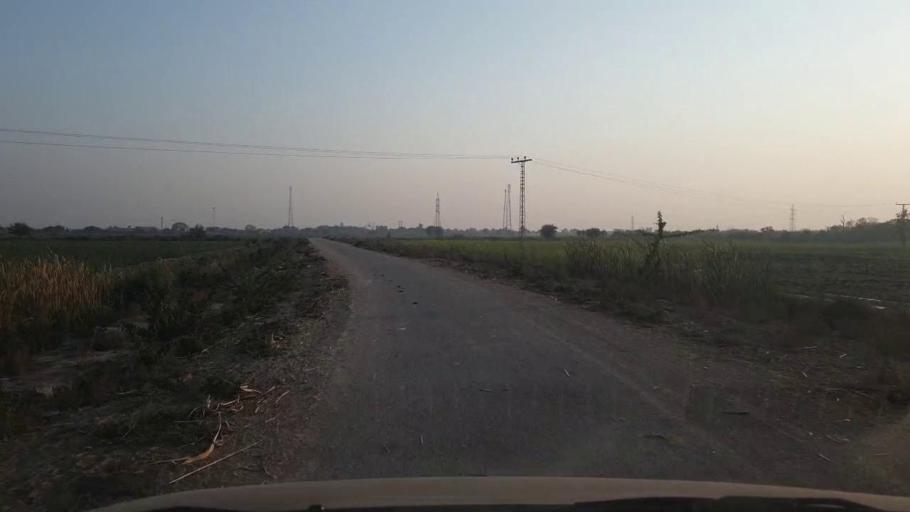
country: PK
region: Sindh
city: Mirwah Gorchani
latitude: 25.3215
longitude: 69.1575
